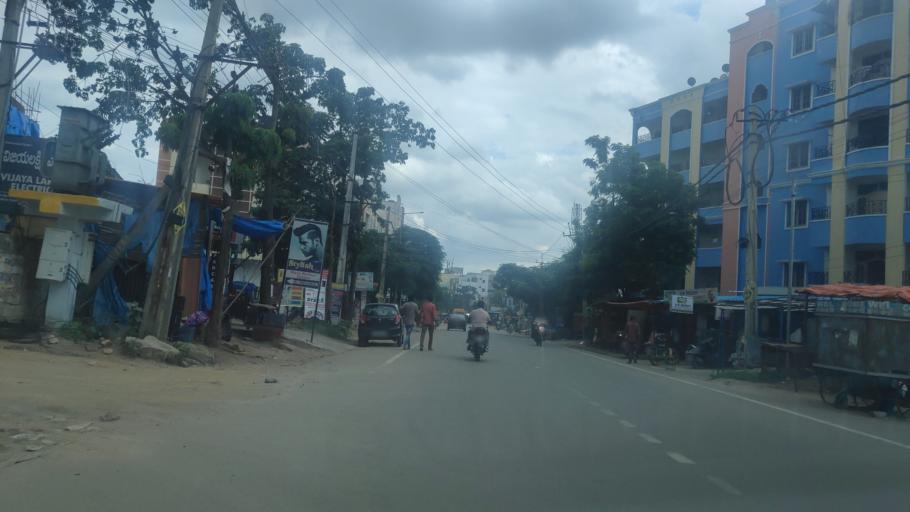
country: IN
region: Telangana
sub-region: Medak
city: Serilingampalle
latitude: 17.5070
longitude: 78.3544
